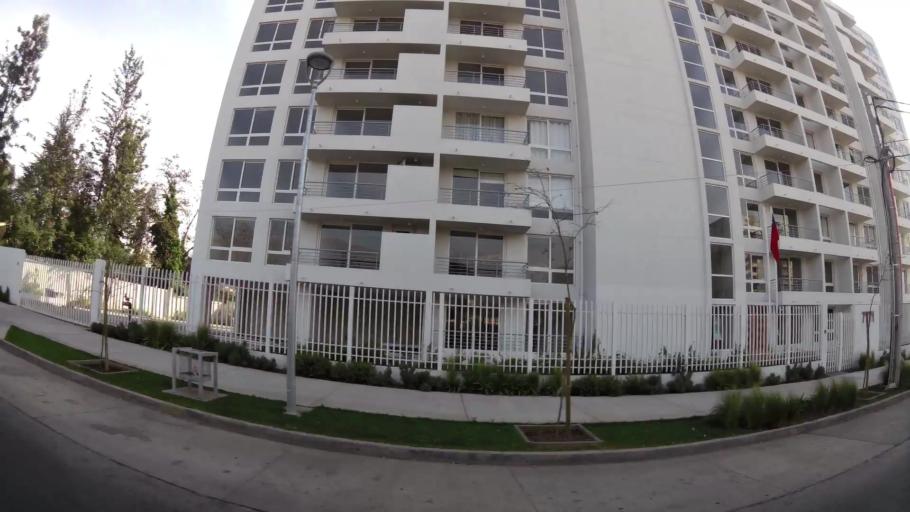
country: CL
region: Santiago Metropolitan
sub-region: Provincia de Santiago
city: Villa Presidente Frei, Nunoa, Santiago, Chile
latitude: -33.5259
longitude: -70.5891
